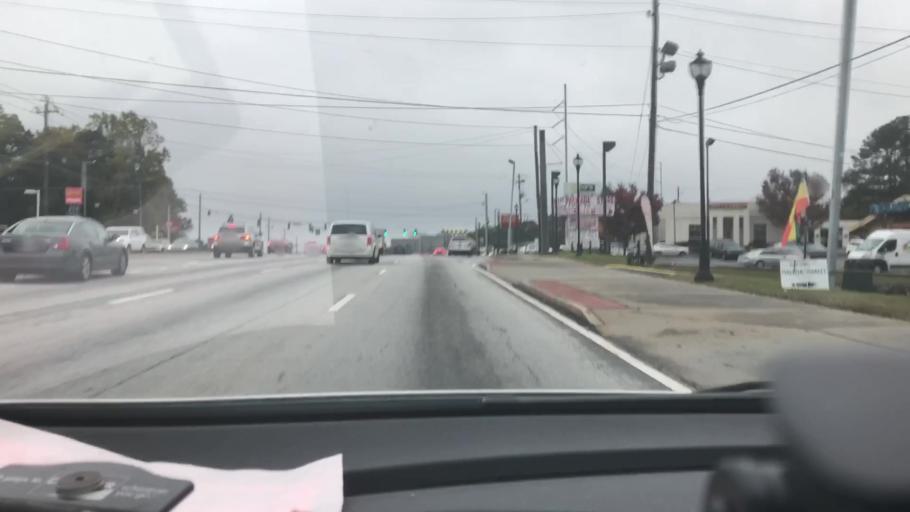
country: US
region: Georgia
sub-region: DeKalb County
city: Clarkston
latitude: 33.7878
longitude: -84.2329
